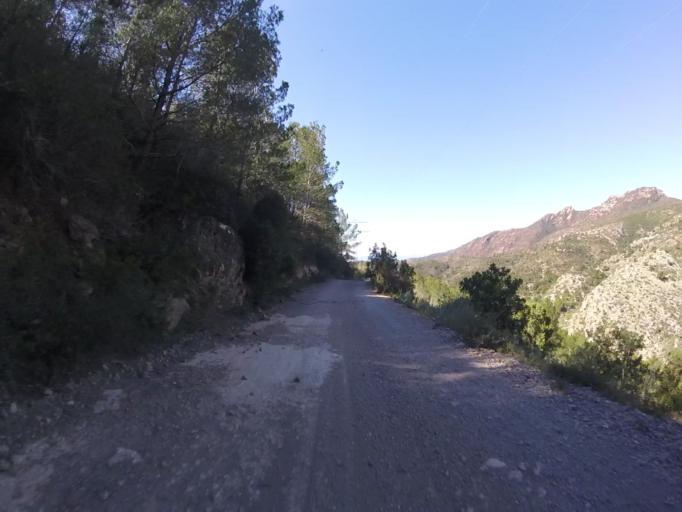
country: ES
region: Valencia
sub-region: Provincia de Castello
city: Benicassim
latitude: 40.0775
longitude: 0.0787
